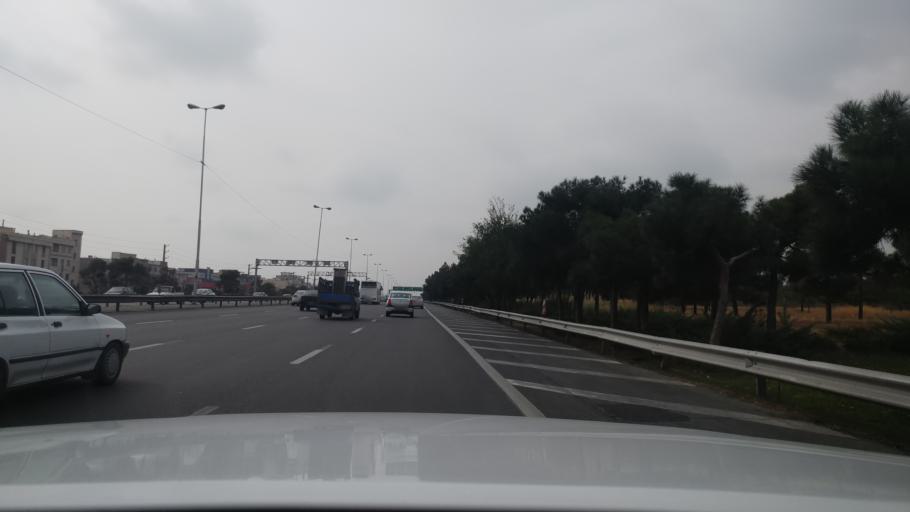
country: IR
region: Tehran
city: Tehran
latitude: 35.7158
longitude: 51.2775
